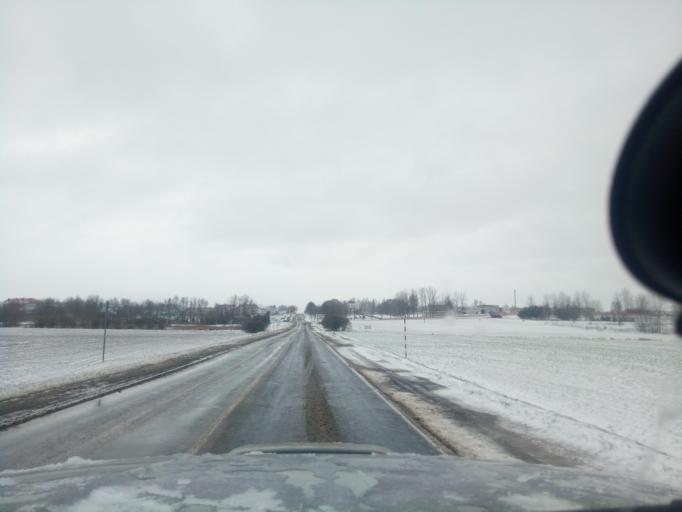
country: BY
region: Minsk
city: Klyetsk
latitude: 53.0827
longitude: 26.6421
